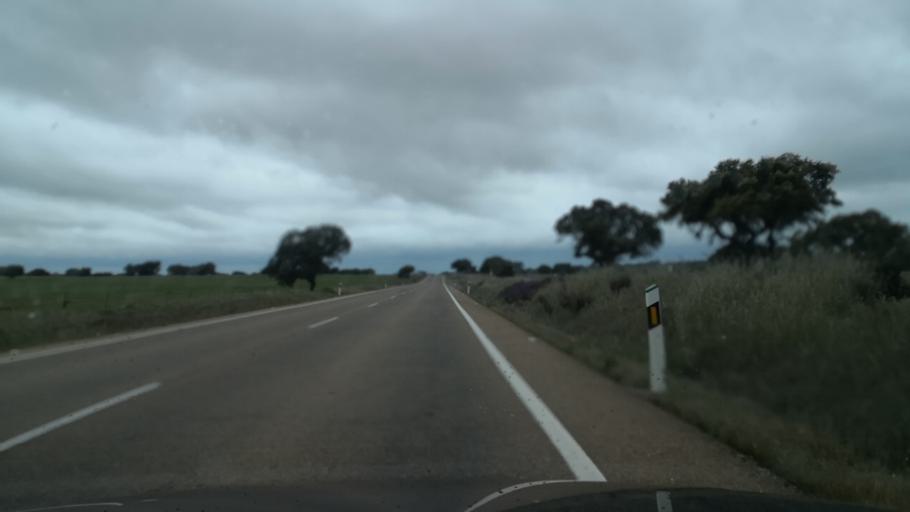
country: ES
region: Extremadura
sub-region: Provincia de Badajoz
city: Villar del Rey
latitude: 39.0198
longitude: -6.8475
